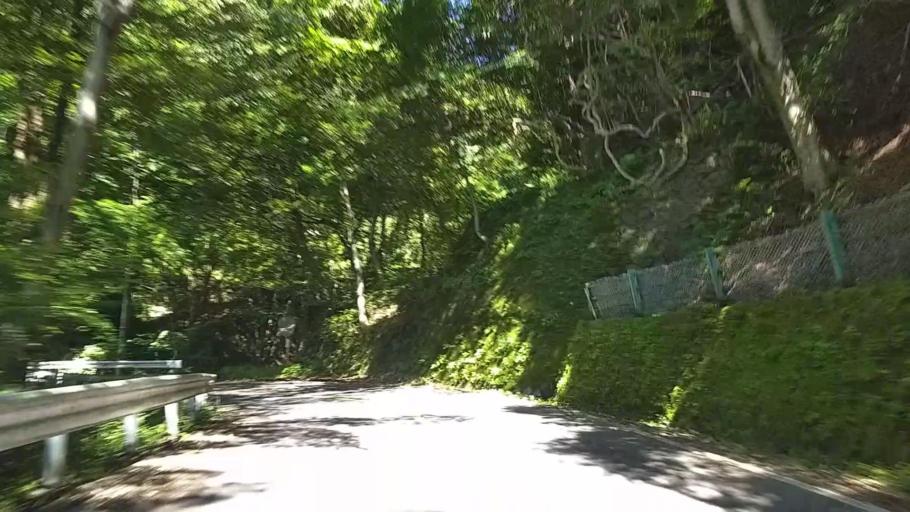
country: JP
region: Gunma
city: Annaka
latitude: 36.3547
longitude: 138.6717
